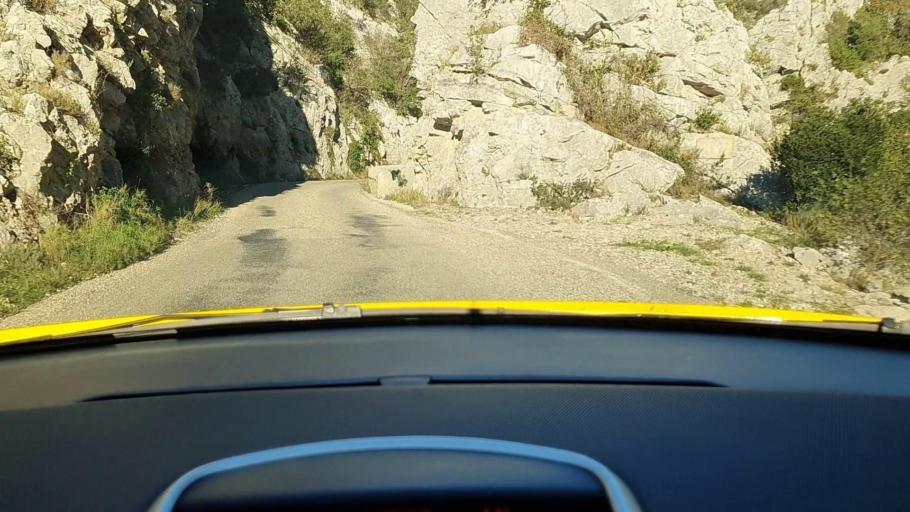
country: FR
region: Languedoc-Roussillon
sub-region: Departement du Gard
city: Saint-Hippolyte-du-Fort
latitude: 43.9605
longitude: 3.8070
